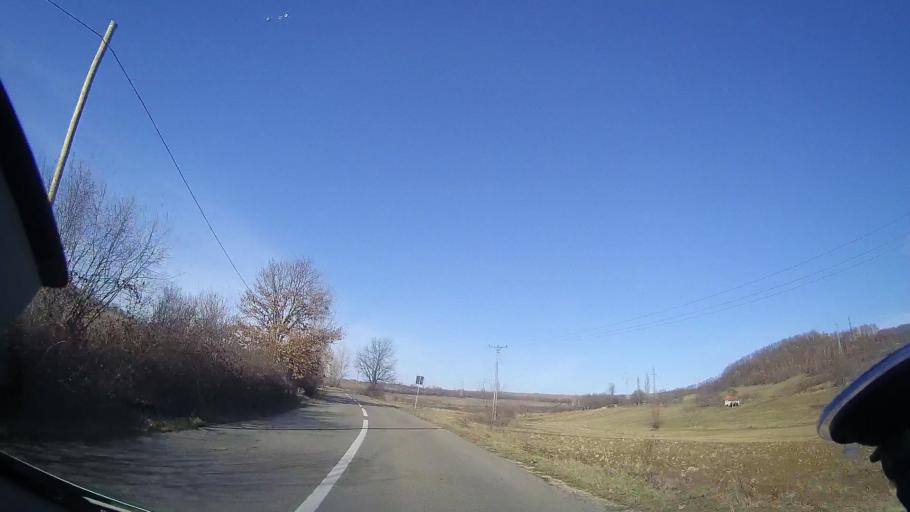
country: RO
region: Bihor
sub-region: Comuna Suncuius
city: Balnaca
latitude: 46.9643
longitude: 22.5526
